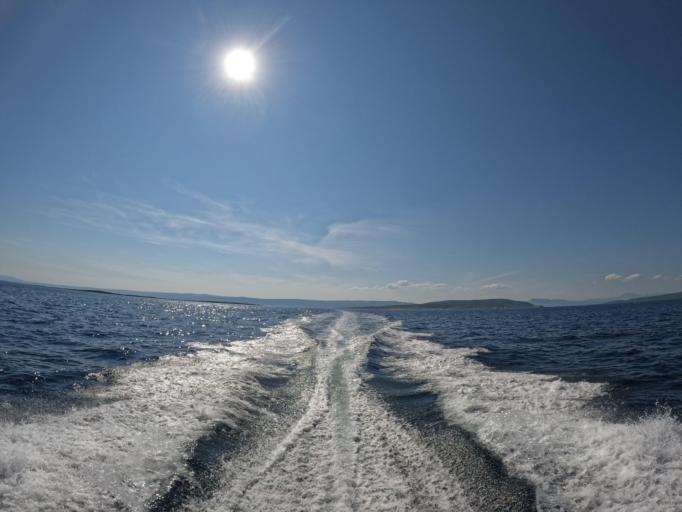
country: HR
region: Primorsko-Goranska
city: Punat
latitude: 44.9541
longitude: 14.5885
